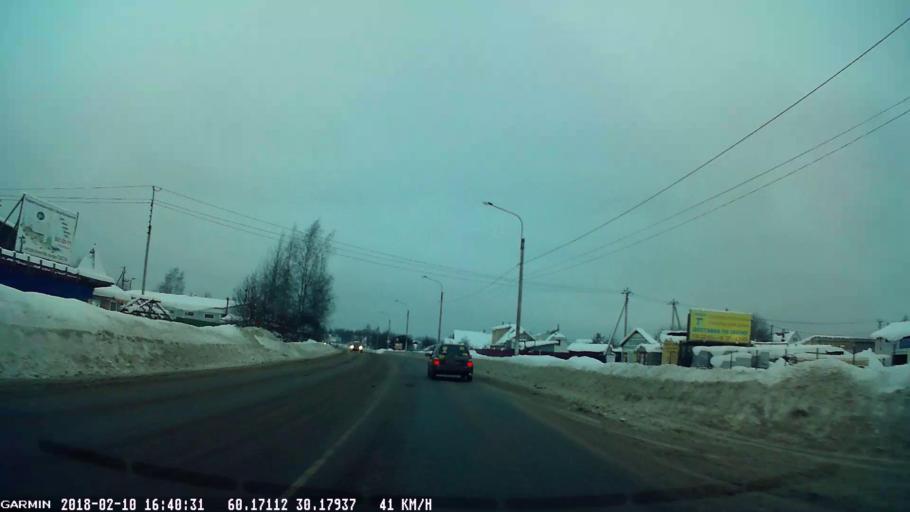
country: RU
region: Leningrad
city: Sertolovo
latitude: 60.1610
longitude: 30.1845
